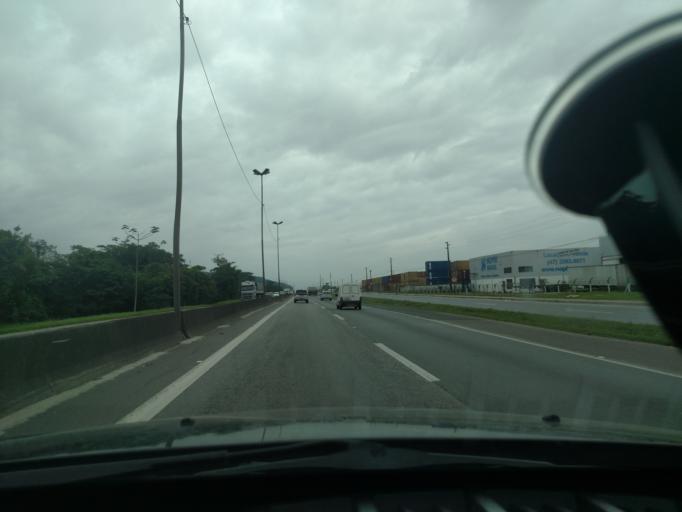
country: BR
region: Santa Catarina
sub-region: Itajai
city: Itajai
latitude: -26.9168
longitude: -48.7102
